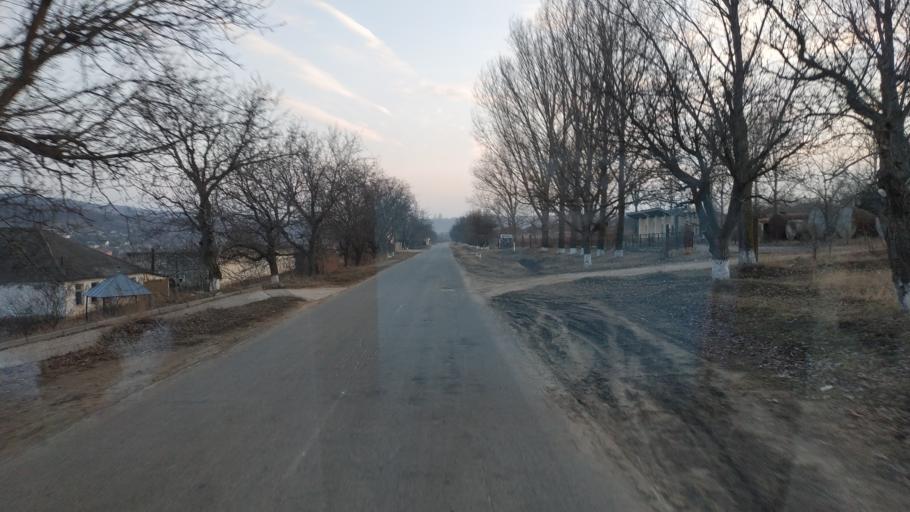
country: MD
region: Hincesti
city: Dancu
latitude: 46.6801
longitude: 28.3353
